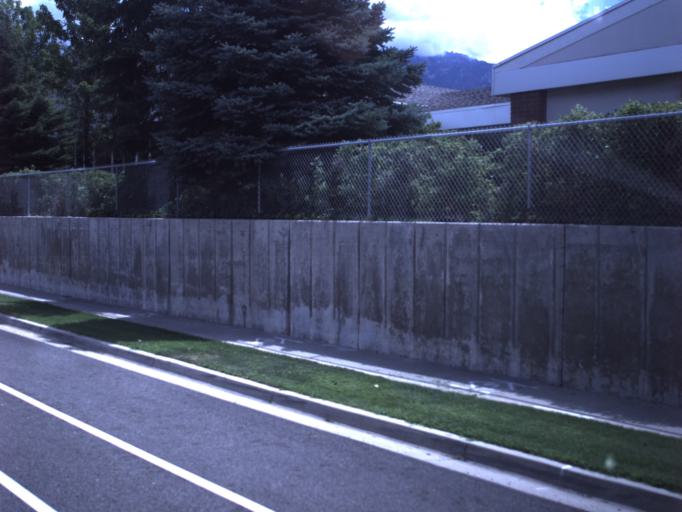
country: US
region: Utah
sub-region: Salt Lake County
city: Sandy Hills
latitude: 40.5803
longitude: -111.8474
